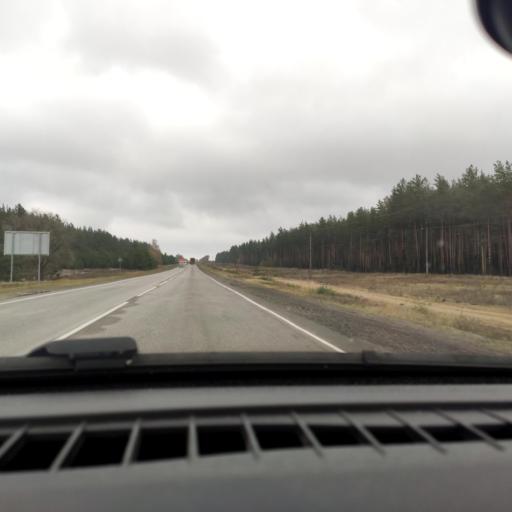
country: RU
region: Voronezj
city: Uryv-Pokrovka
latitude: 51.0515
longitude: 38.9856
